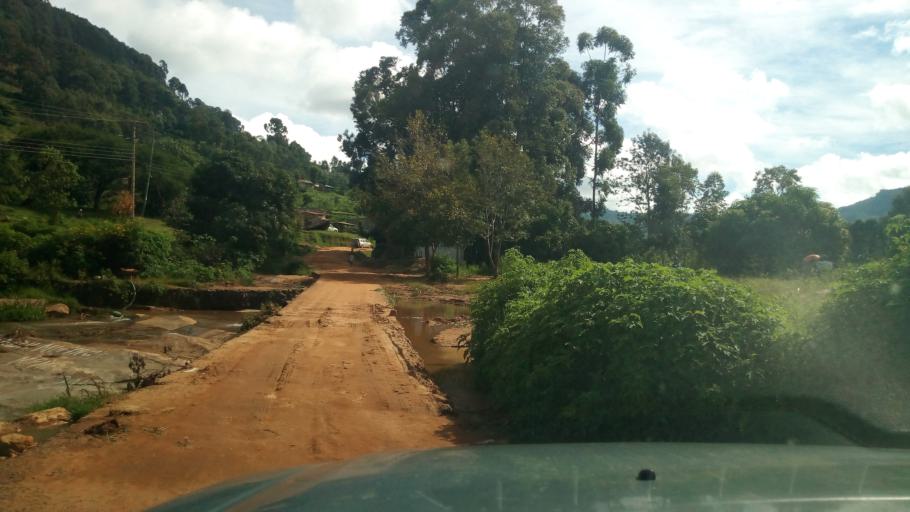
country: KE
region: Makueni
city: Wote
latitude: -1.7066
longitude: 37.4464
